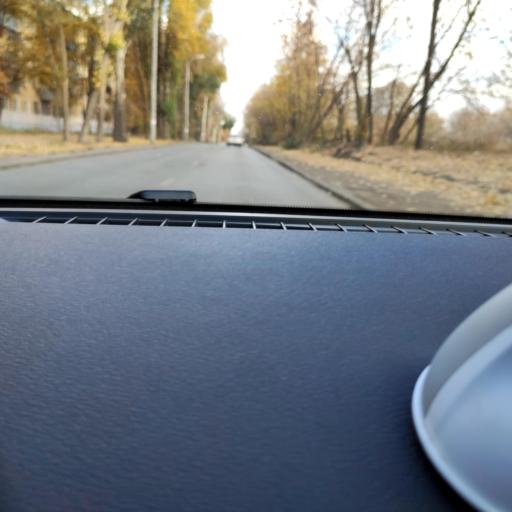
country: RU
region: Samara
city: Samara
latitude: 53.2238
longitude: 50.2081
